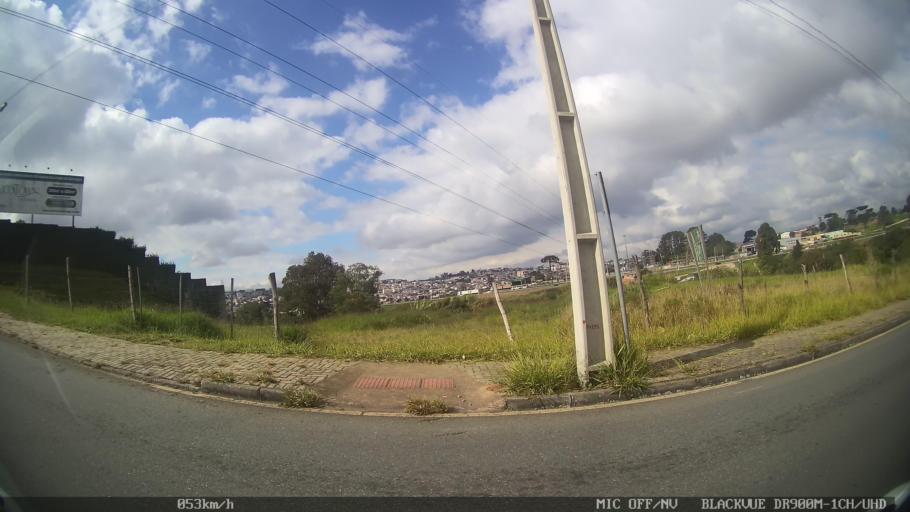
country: BR
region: Parana
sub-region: Pinhais
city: Pinhais
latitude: -25.3789
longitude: -49.2011
